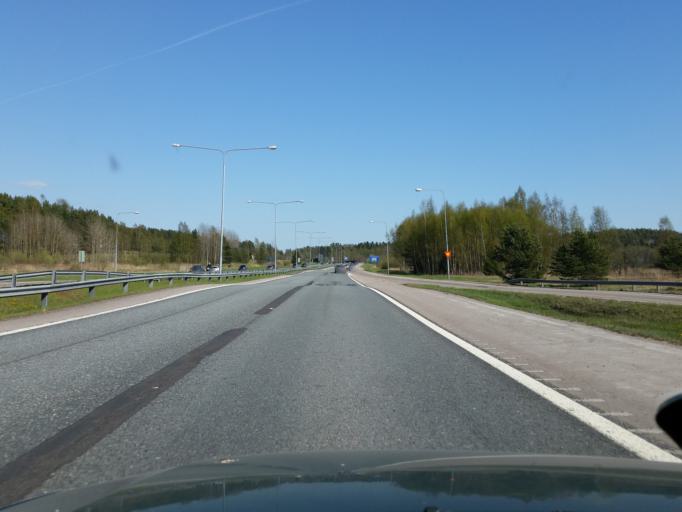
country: FI
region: Uusimaa
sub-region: Helsinki
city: Kirkkonummi
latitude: 60.1164
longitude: 24.4481
